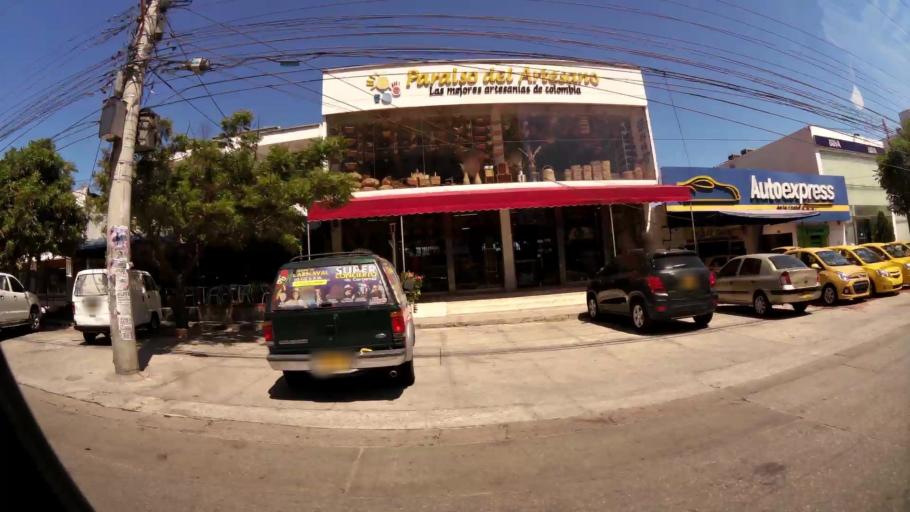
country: CO
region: Atlantico
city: Barranquilla
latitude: 10.9948
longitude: -74.8126
